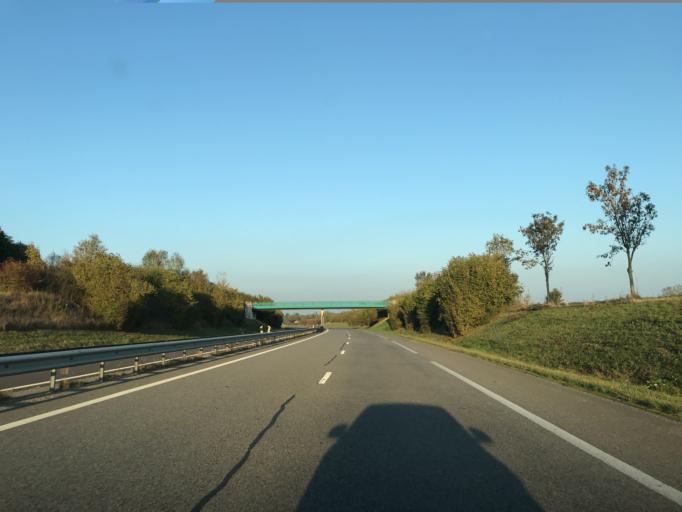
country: FR
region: Lower Normandy
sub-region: Departement de l'Orne
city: Valframbert
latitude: 48.4558
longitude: 0.1375
